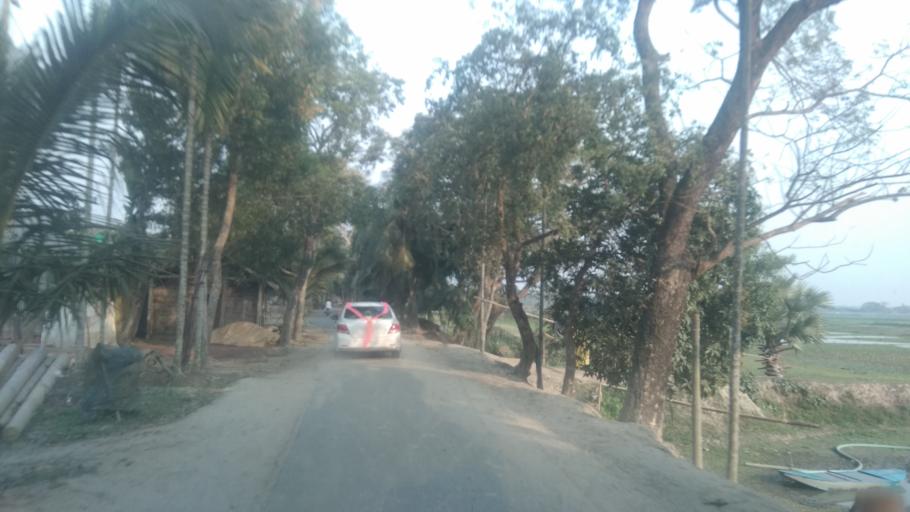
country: BD
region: Dhaka
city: Netrakona
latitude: 24.7757
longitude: 90.6038
